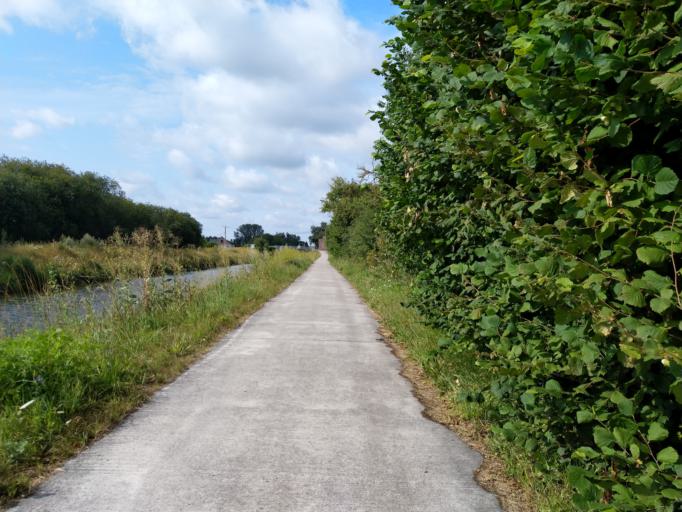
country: BE
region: Wallonia
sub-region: Province du Hainaut
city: Beloeil
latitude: 50.5639
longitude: 3.7602
